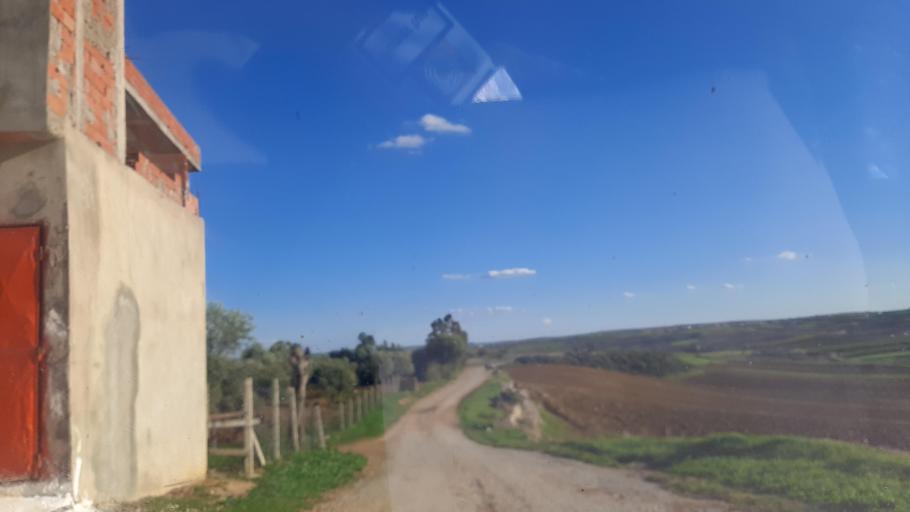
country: TN
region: Nabul
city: El Mida
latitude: 36.8372
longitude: 10.8324
